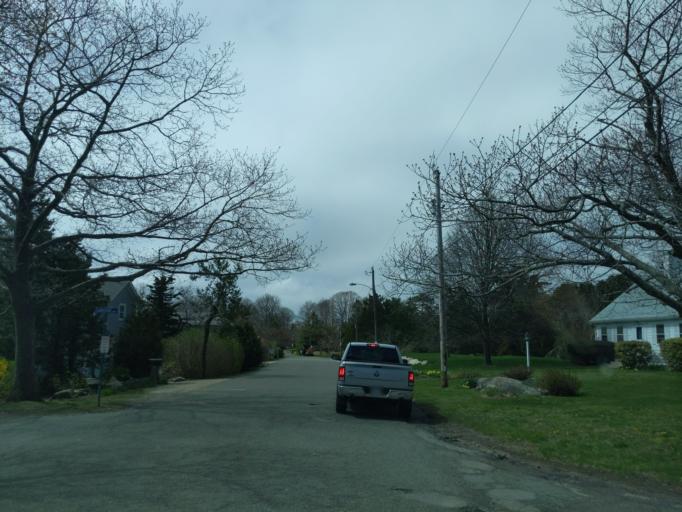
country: US
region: Massachusetts
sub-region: Essex County
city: Rockport
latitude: 42.6385
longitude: -70.6018
